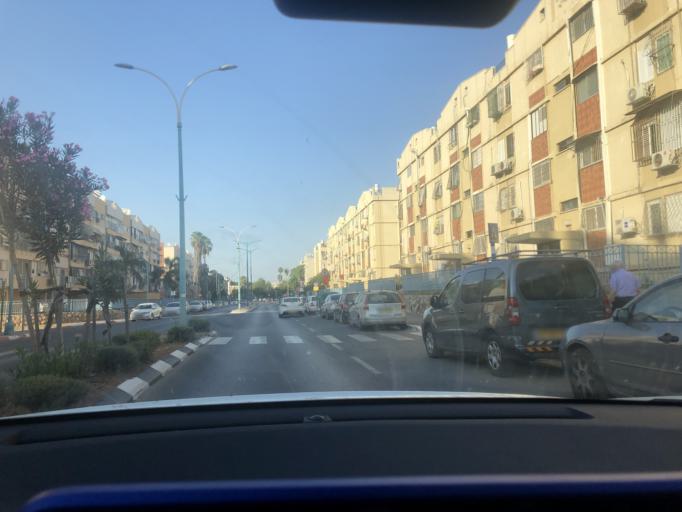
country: IL
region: Central District
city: Lod
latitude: 31.9495
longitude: 34.8832
